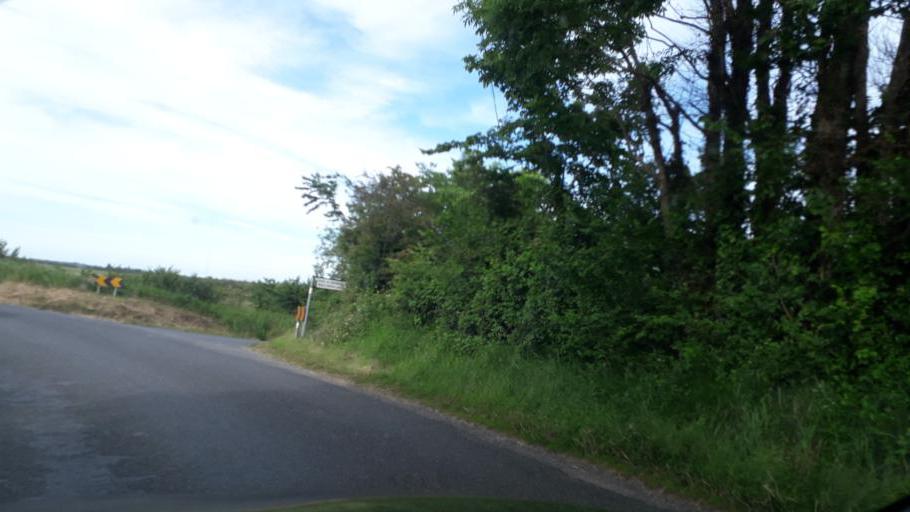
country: IE
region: Leinster
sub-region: Loch Garman
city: Courtown
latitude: 52.5344
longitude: -6.2556
